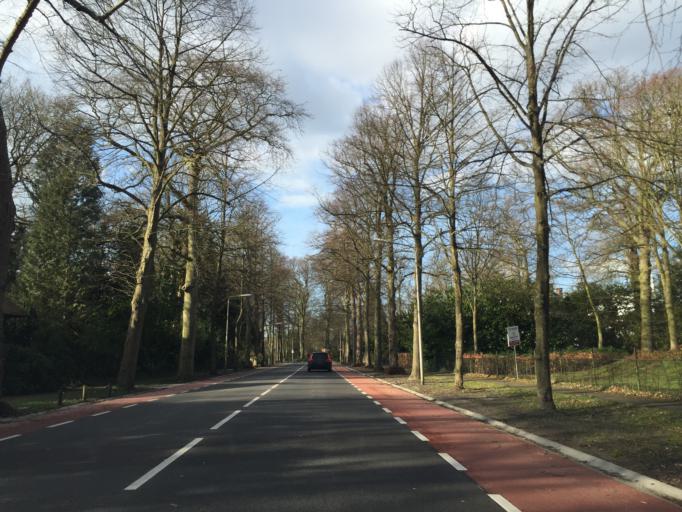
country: NL
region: South Holland
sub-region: Gemeente Wassenaar
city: Wassenaar
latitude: 52.1166
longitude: 4.3719
